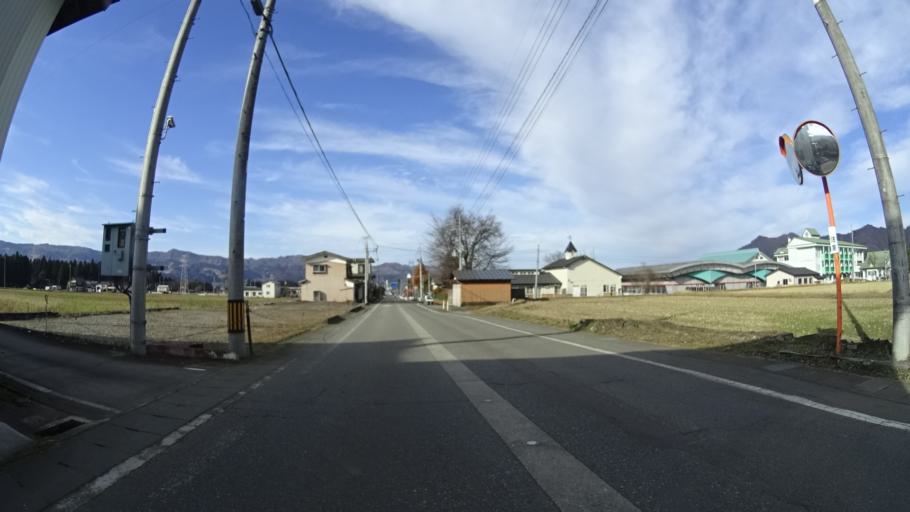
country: JP
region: Niigata
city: Shiozawa
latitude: 37.0215
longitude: 138.8750
